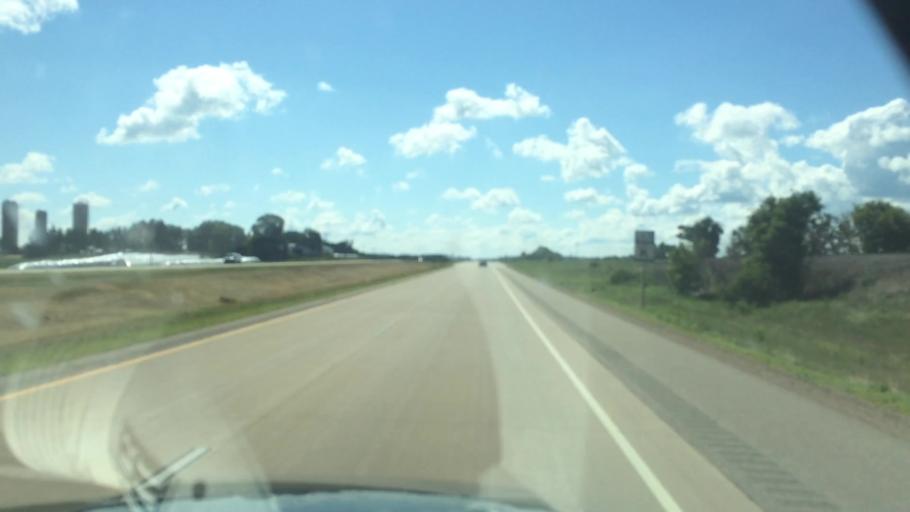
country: US
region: Wisconsin
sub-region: Portage County
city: Amherst
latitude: 44.4961
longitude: -89.3701
